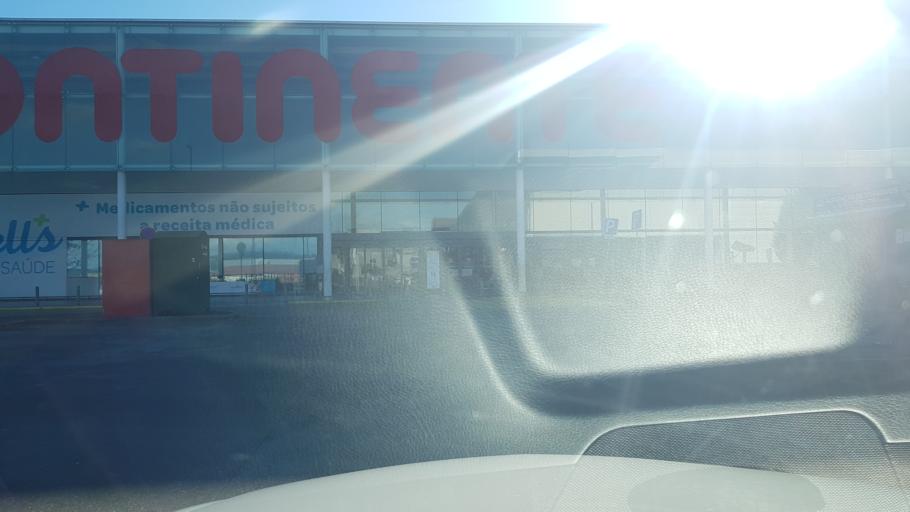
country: PT
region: Santarem
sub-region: Torres Novas
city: Torres Novas
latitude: 39.4625
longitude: -8.5325
